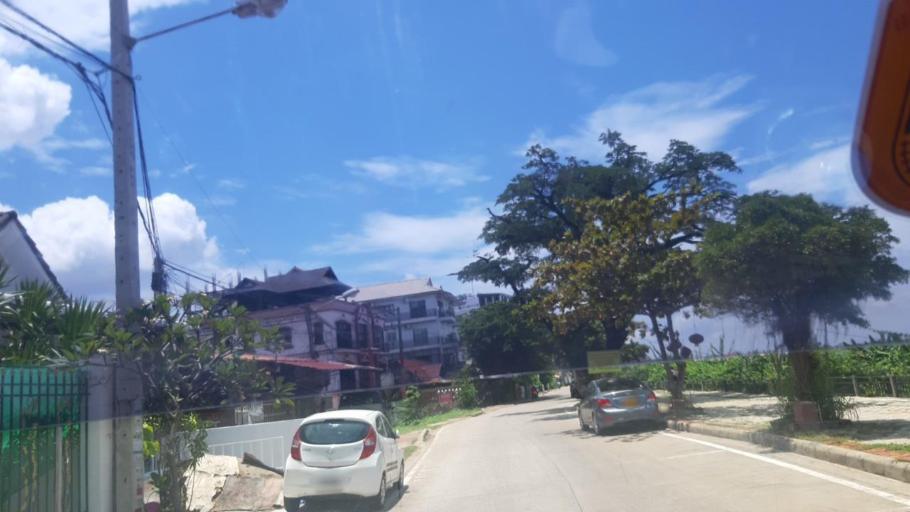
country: LA
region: Vientiane
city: Vientiane
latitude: 17.9663
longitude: 102.5946
